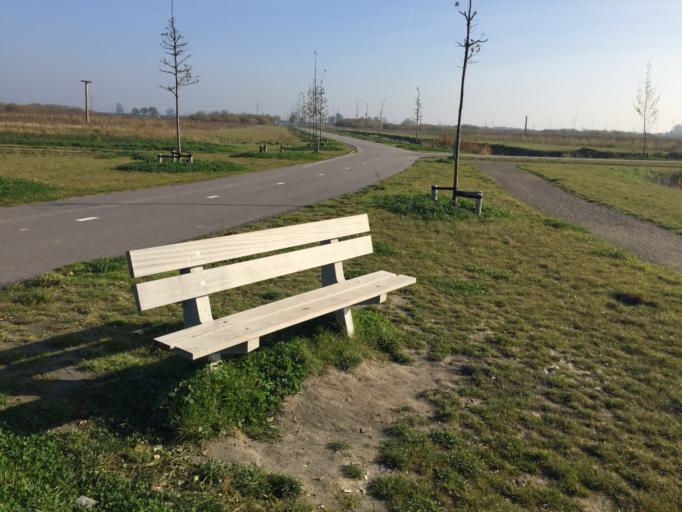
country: NL
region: South Holland
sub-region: Gemeente Rijnwoude
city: Benthuizen
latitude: 52.0696
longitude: 4.5481
